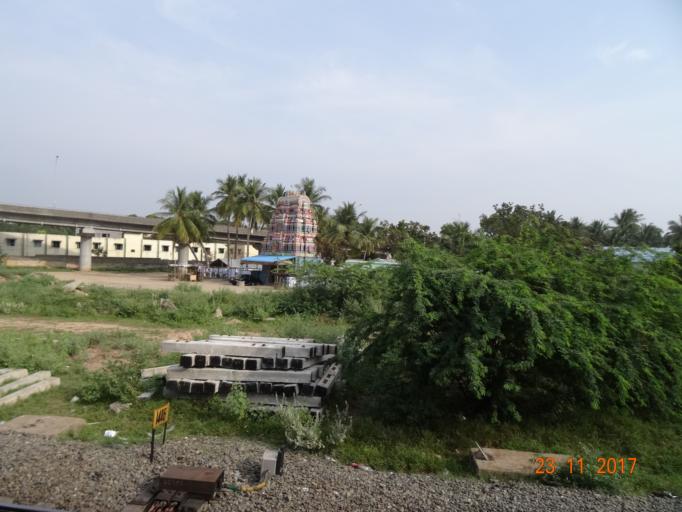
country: IN
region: Tamil Nadu
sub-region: Coimbatore
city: Irugur
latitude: 11.0127
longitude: 77.0657
